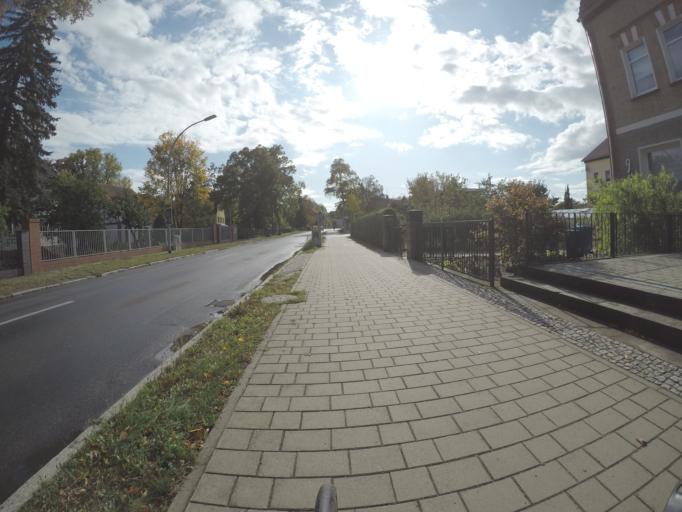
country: DE
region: Brandenburg
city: Rehfelde
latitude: 52.5330
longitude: 13.8450
